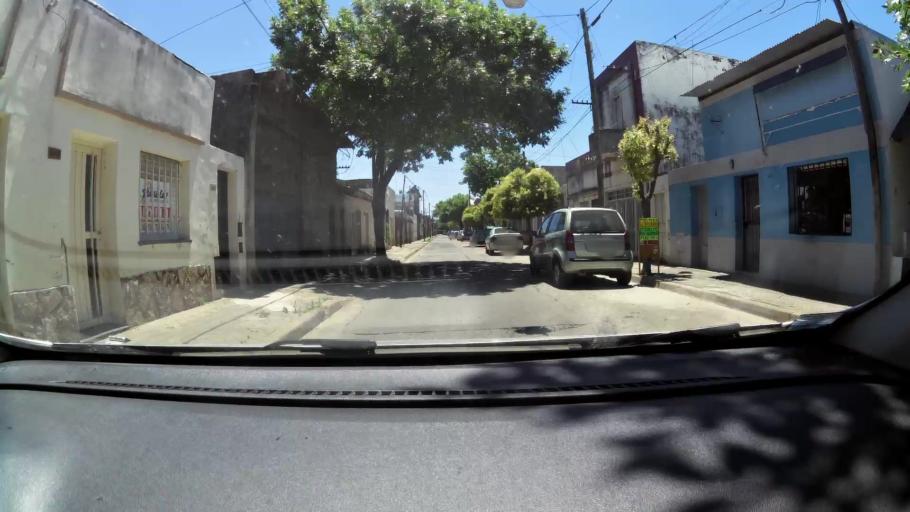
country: AR
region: Santa Fe
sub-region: Departamento de Rosario
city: Rosario
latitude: -32.9446
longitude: -60.6956
